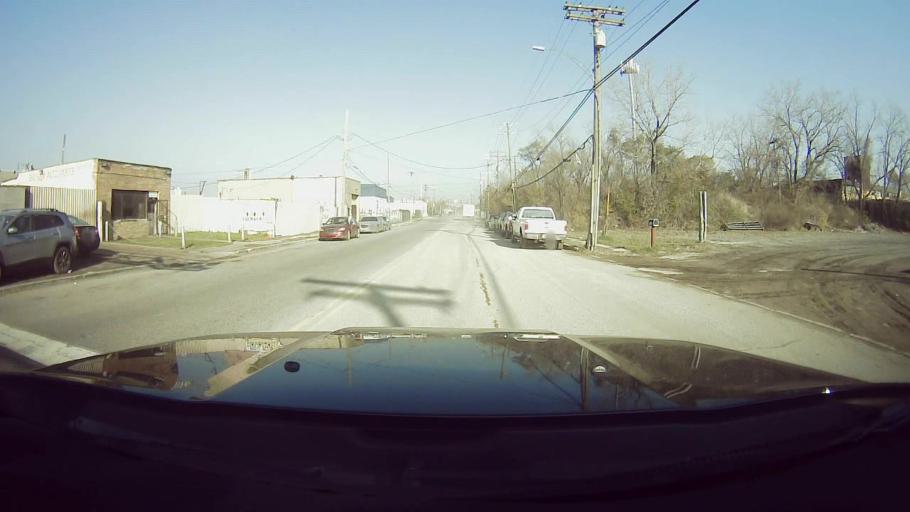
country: US
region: Michigan
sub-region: Oakland County
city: Oak Park
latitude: 42.3933
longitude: -83.1689
